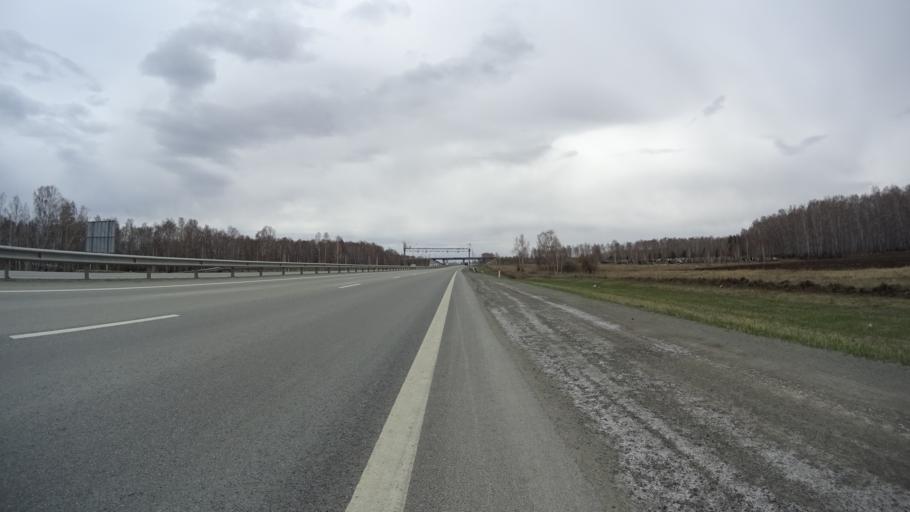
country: RU
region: Chelyabinsk
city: Yemanzhelinka
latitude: 54.8194
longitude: 61.3088
